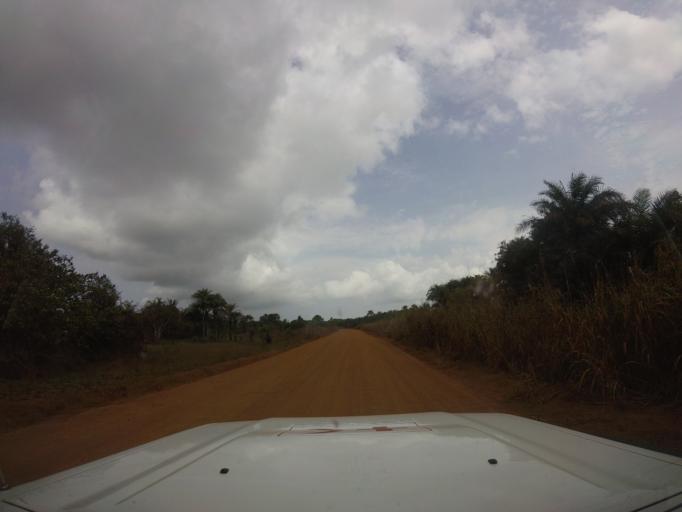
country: LR
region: Grand Cape Mount
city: Robertsport
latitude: 6.7025
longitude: -11.2903
